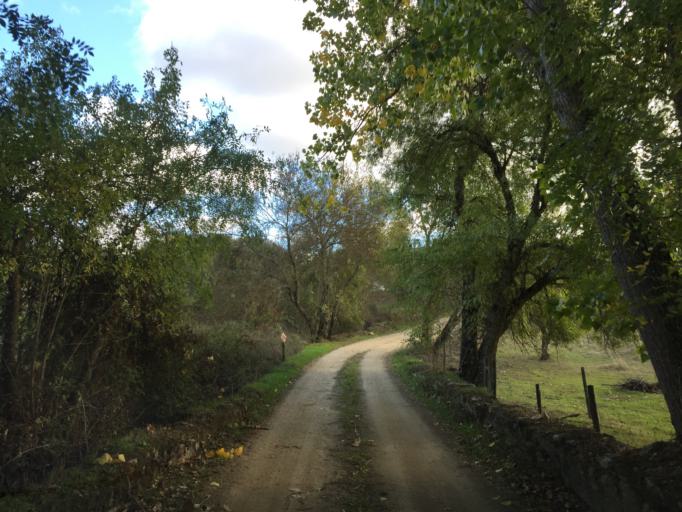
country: PT
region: Portalegre
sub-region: Alter do Chao
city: Alter do Chao
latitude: 39.2711
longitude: -7.6408
